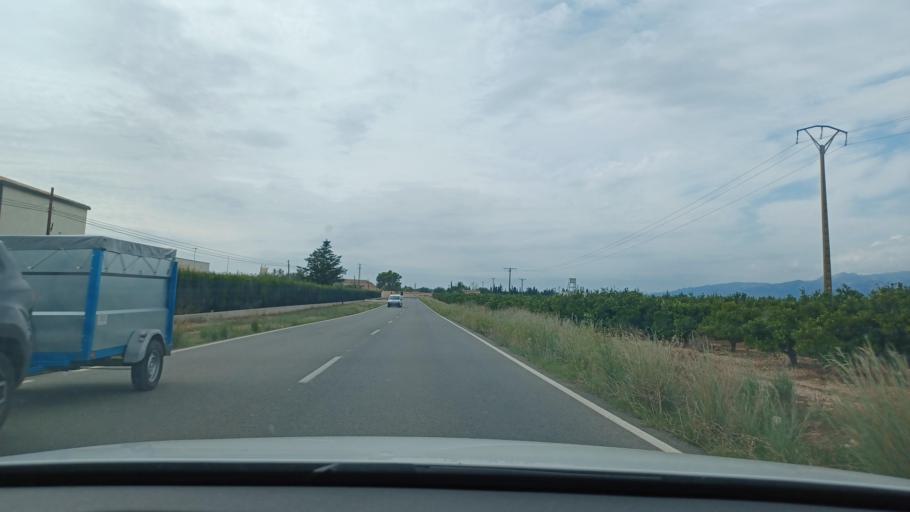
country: ES
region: Catalonia
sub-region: Provincia de Tarragona
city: Tortosa
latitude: 40.7665
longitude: 0.5076
